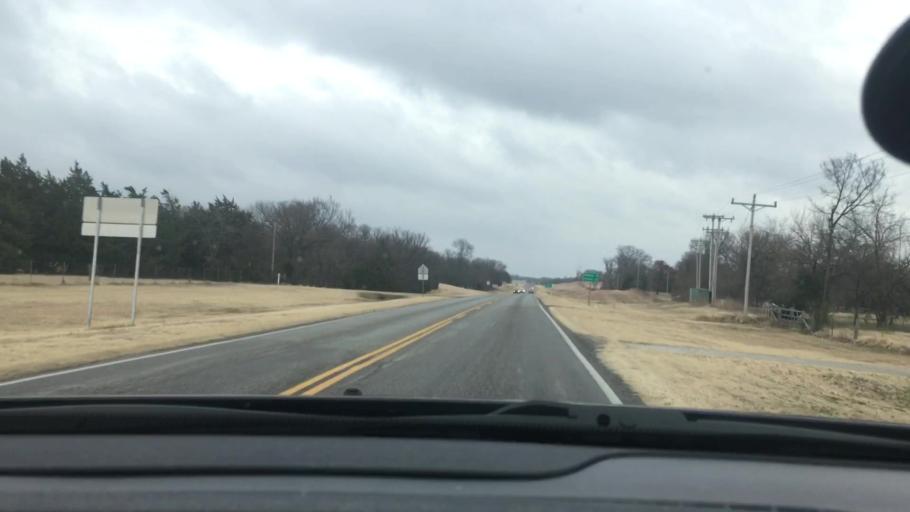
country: US
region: Oklahoma
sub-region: Johnston County
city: Tishomingo
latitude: 34.2305
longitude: -96.6587
